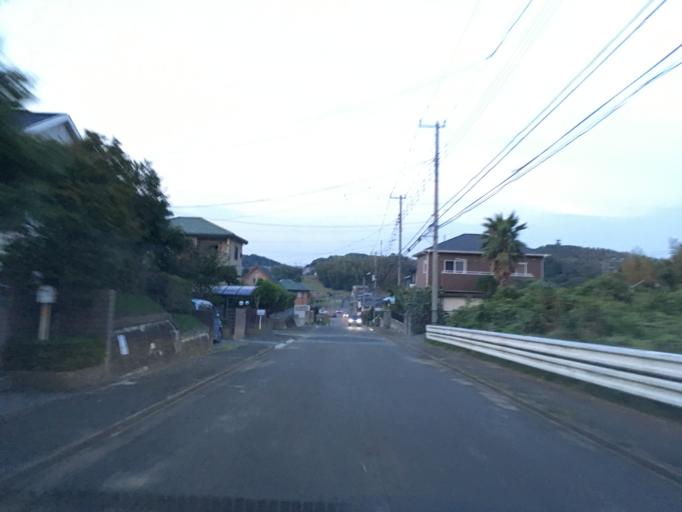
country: JP
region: Chiba
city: Kimitsu
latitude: 35.3419
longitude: 139.9121
